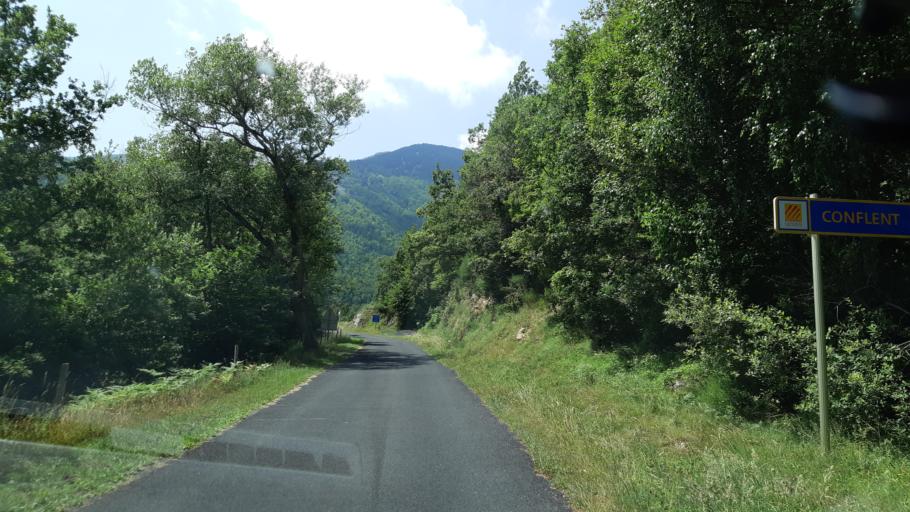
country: FR
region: Languedoc-Roussillon
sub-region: Departement des Pyrenees-Orientales
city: Arles
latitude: 42.5364
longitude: 2.5662
